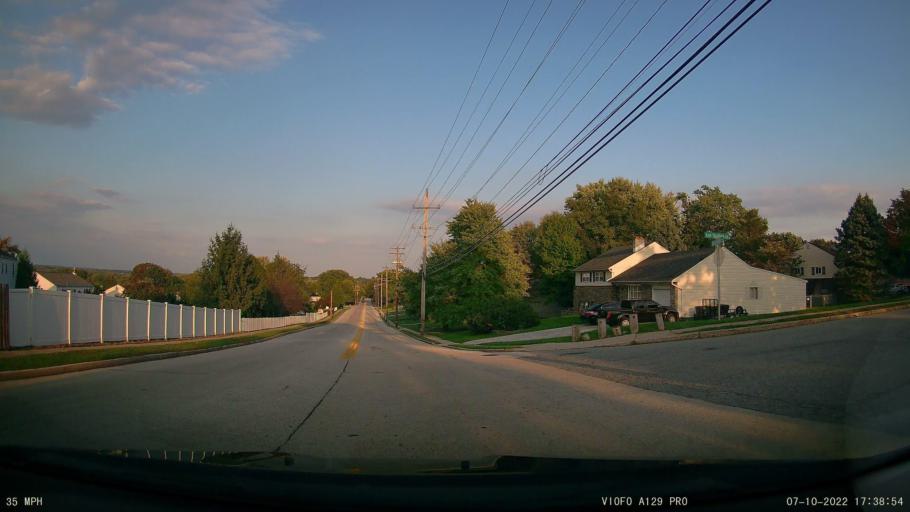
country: US
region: Pennsylvania
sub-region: Montgomery County
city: King of Prussia
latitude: 40.1022
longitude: -75.3915
